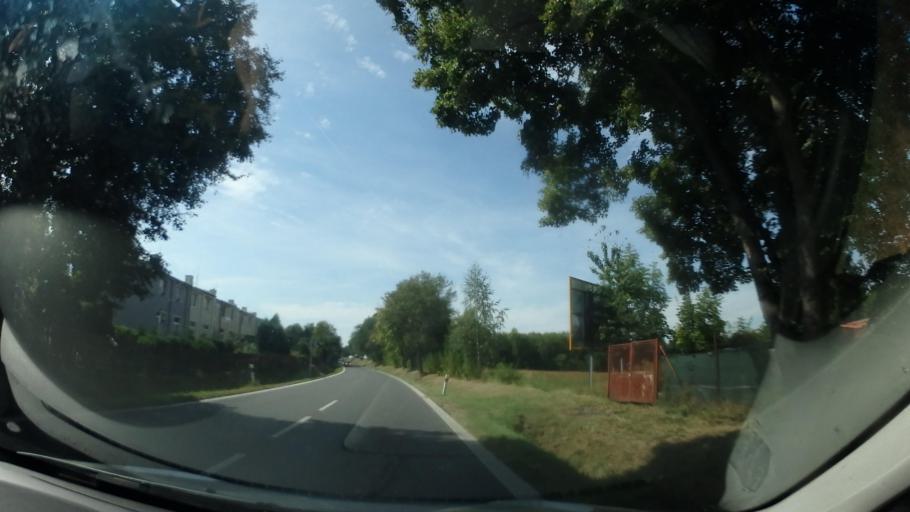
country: CZ
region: Jihocesky
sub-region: Okres Pisek
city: Pisek
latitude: 49.3106
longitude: 14.1251
